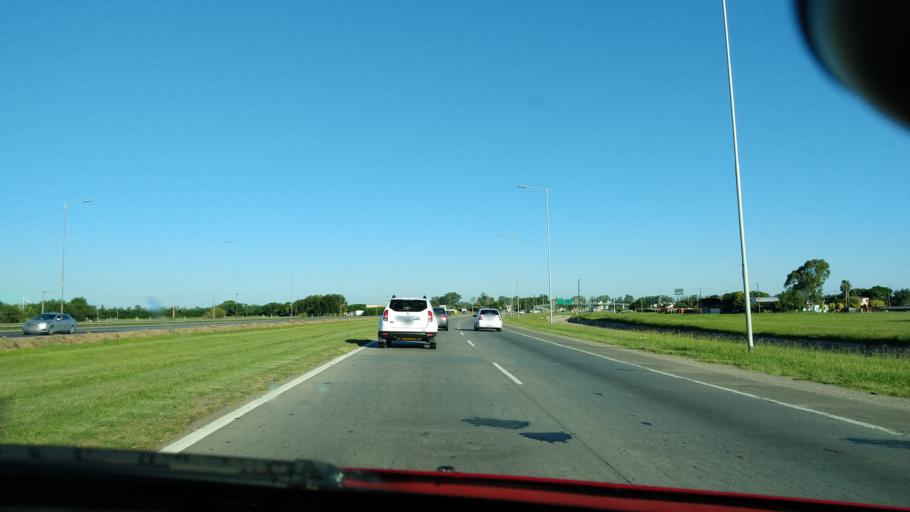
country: AR
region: Cordoba
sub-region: Departamento de Capital
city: Cordoba
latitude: -31.3646
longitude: -64.1343
